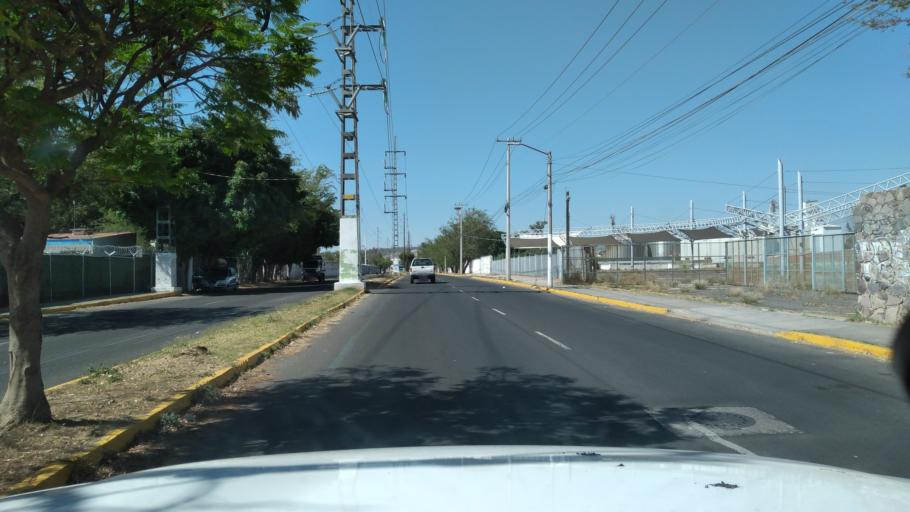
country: MX
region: Jalisco
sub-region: Zapopan
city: Zapopan
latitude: 20.7338
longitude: -103.3762
